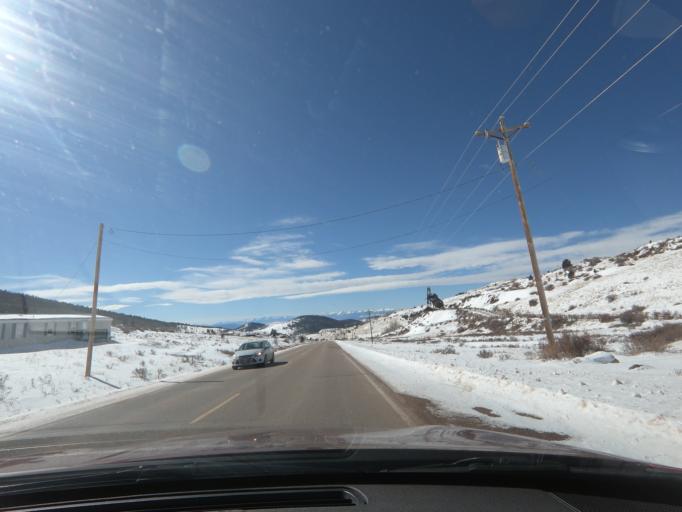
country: US
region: Colorado
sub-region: Teller County
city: Cripple Creek
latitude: 38.7261
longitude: -105.1223
